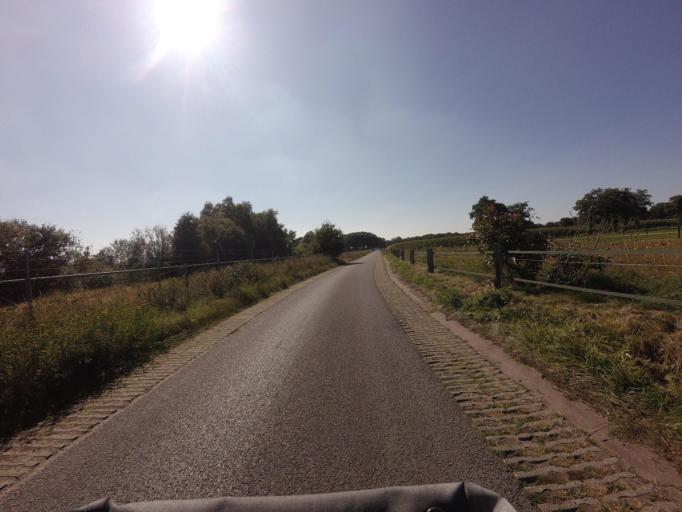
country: DE
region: Lower Saxony
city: Wielen
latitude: 52.5188
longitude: 6.6999
